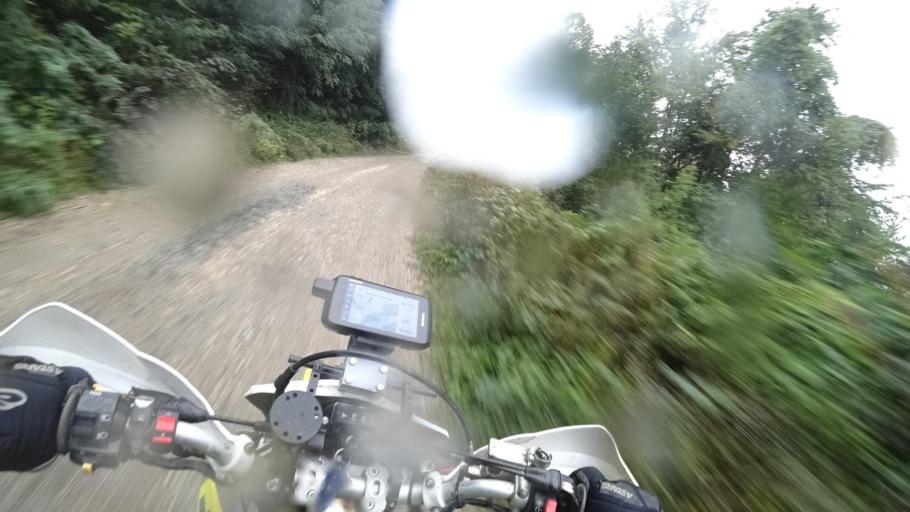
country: BA
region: Republika Srpska
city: Maricka
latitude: 44.8097
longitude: 16.8051
